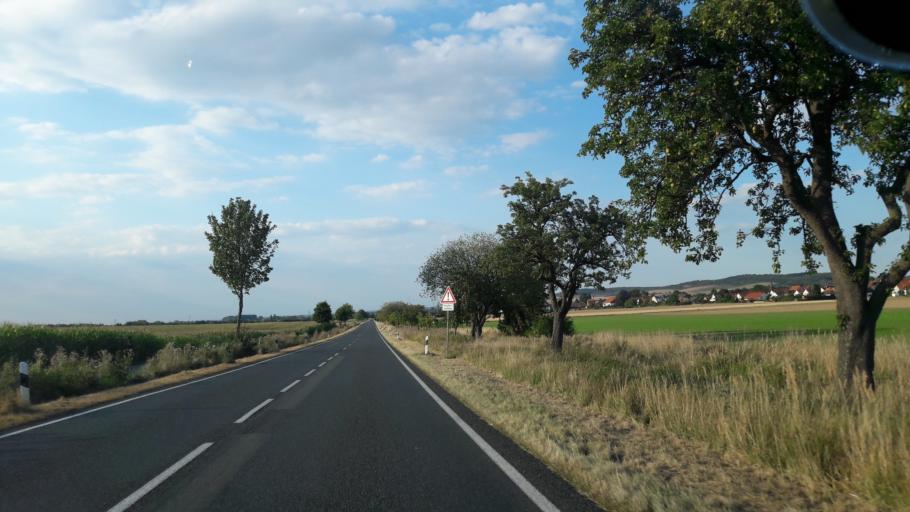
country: DE
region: Lower Saxony
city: Diekholzen
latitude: 52.1371
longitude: 9.8741
